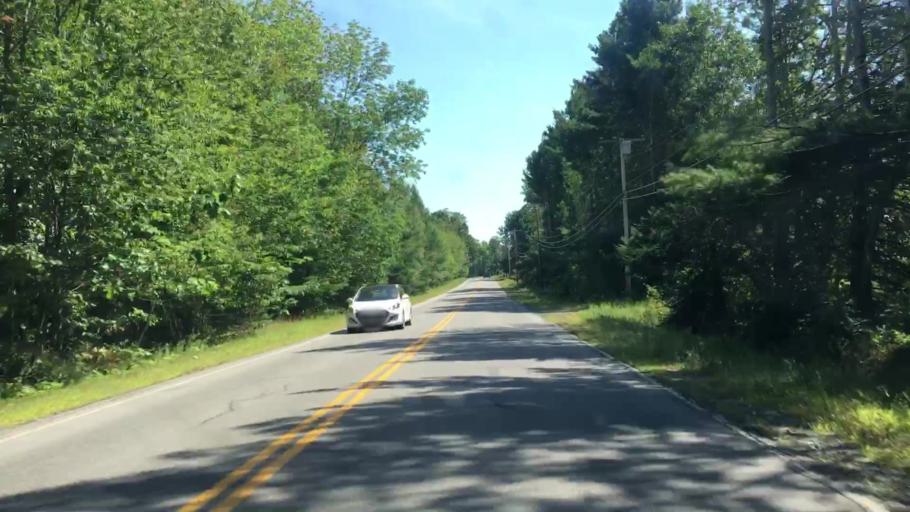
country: US
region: Maine
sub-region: Penobscot County
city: Bradford
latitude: 45.1734
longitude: -68.8521
